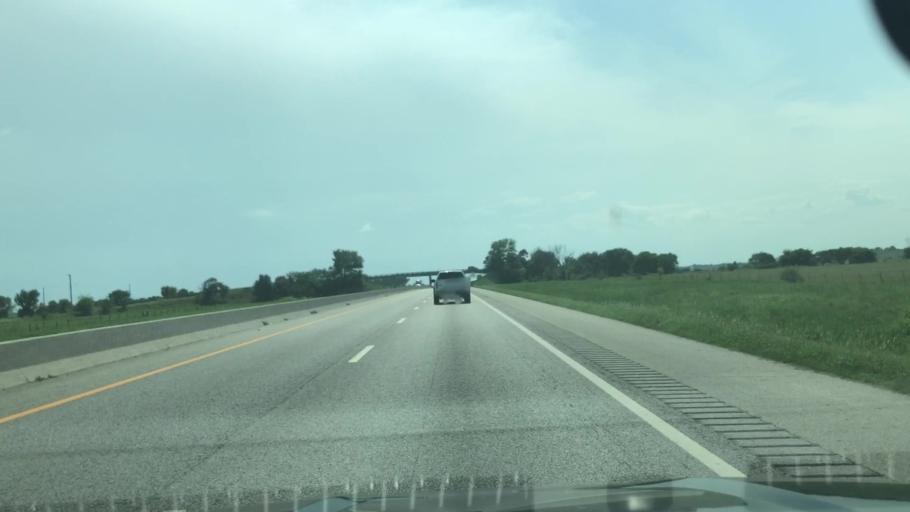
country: US
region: Oklahoma
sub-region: Ottawa County
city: Afton
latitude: 36.7011
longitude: -94.9931
